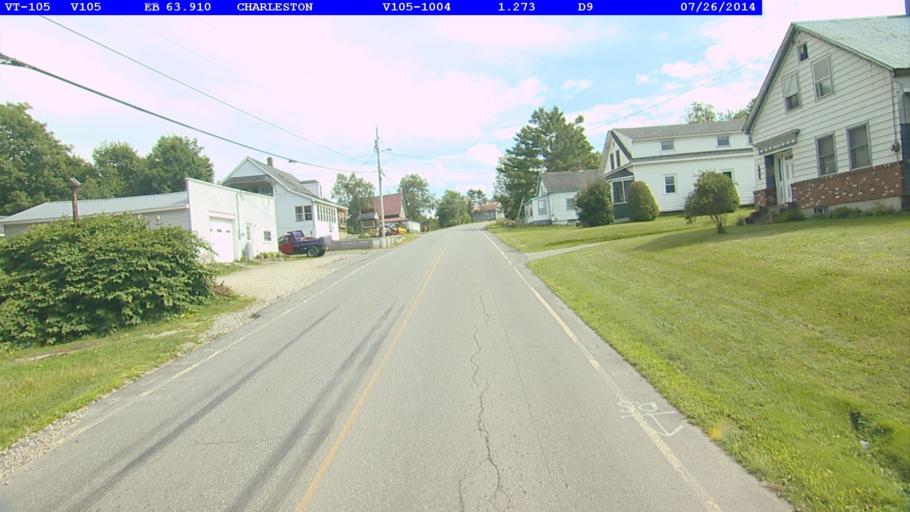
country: US
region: Vermont
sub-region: Orleans County
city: Newport
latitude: 44.8966
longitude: -72.0567
